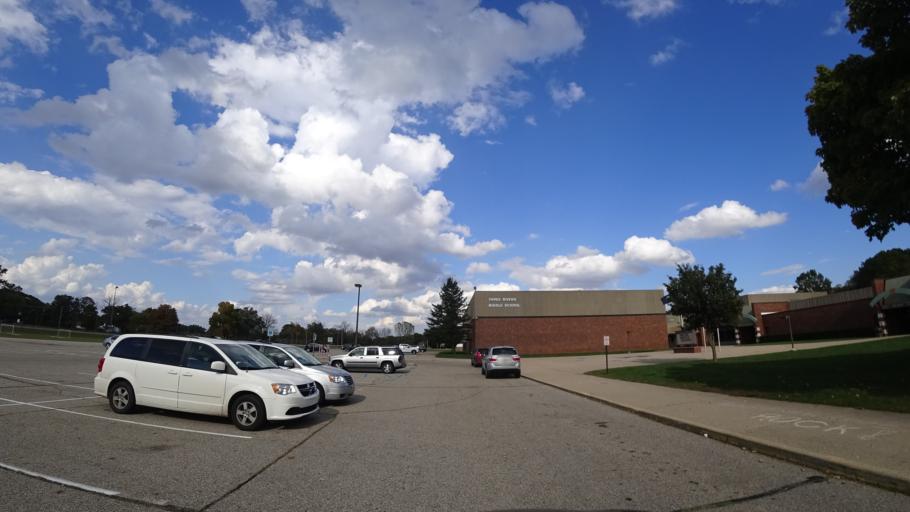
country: US
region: Michigan
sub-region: Saint Joseph County
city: Three Rivers
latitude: 41.9526
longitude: -85.6183
